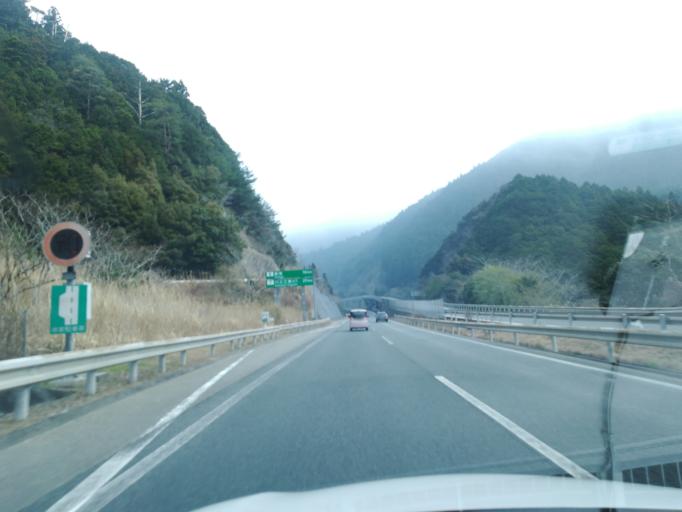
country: JP
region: Ehime
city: Kawanoecho
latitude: 33.7867
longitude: 133.6635
